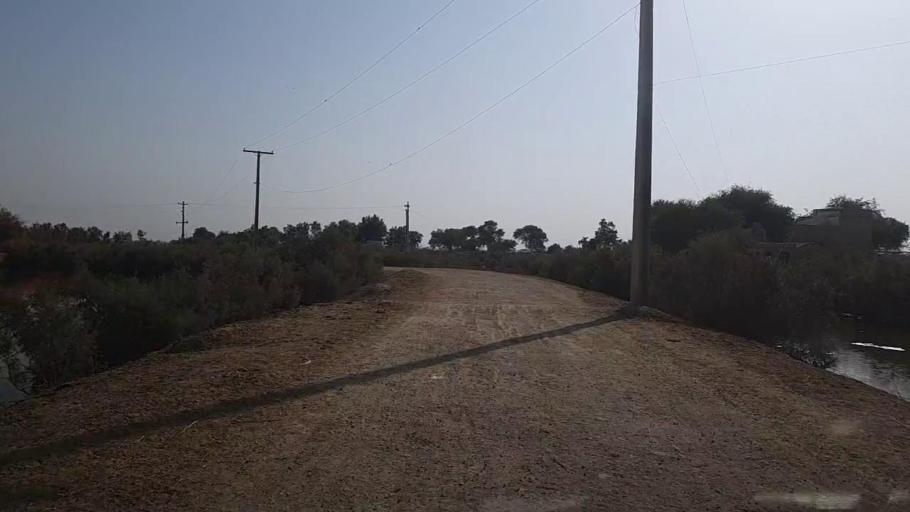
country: PK
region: Sindh
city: Kandhkot
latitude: 28.3815
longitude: 69.3355
